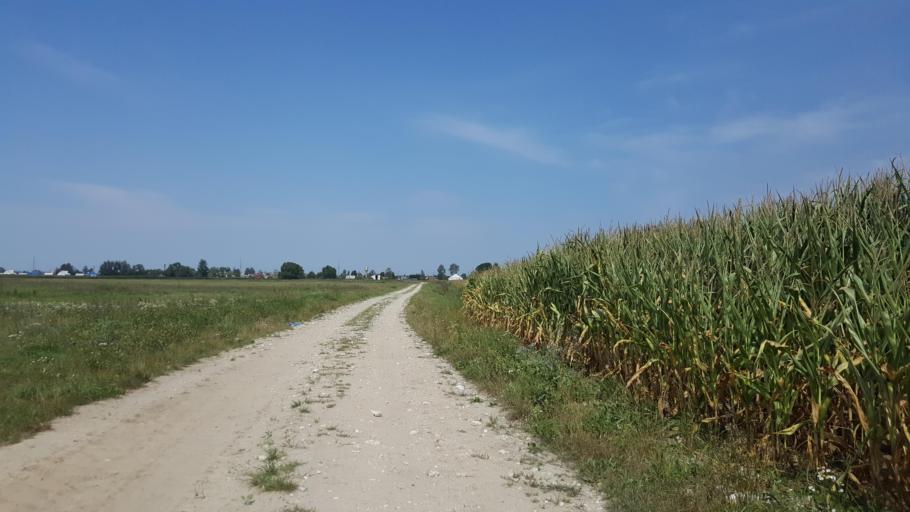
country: PL
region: Podlasie
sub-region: Powiat hajnowski
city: Czeremcha
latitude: 52.4877
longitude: 23.5726
